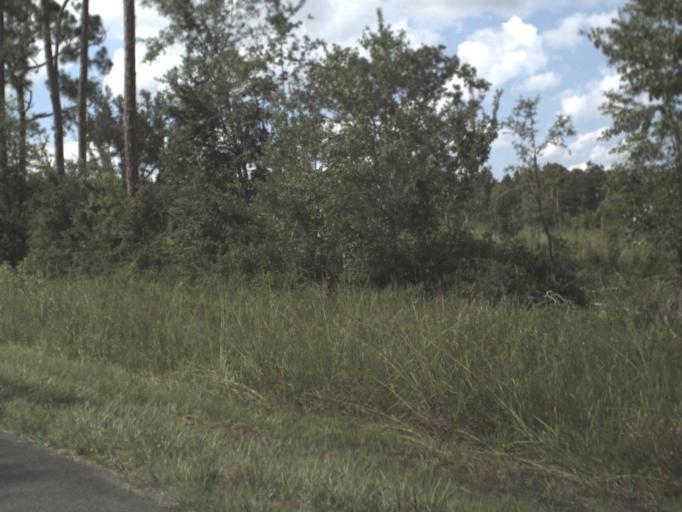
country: US
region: Florida
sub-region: Taylor County
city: Perry
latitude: 30.3561
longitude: -83.6534
